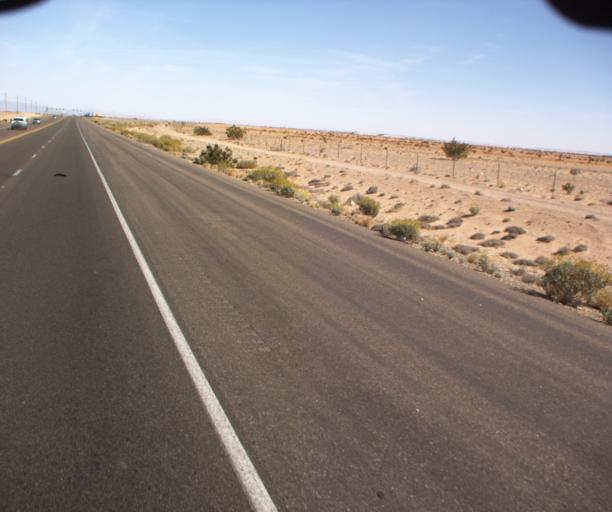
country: MX
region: Sonora
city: San Luis Rio Colorado
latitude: 32.4947
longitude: -114.7077
